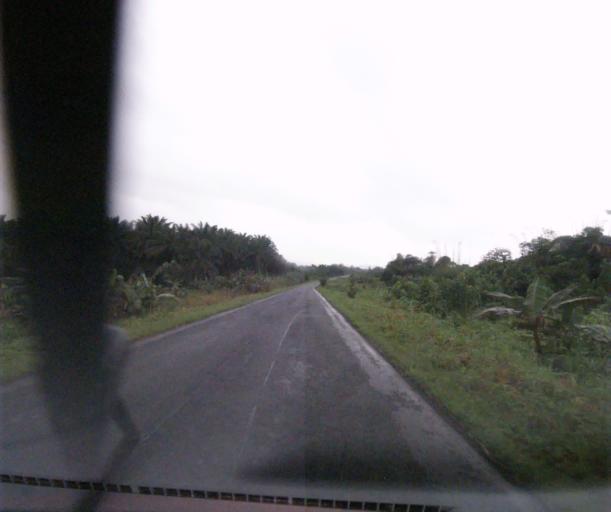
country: CM
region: South-West Province
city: Idenao
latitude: 4.1951
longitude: 9.0030
